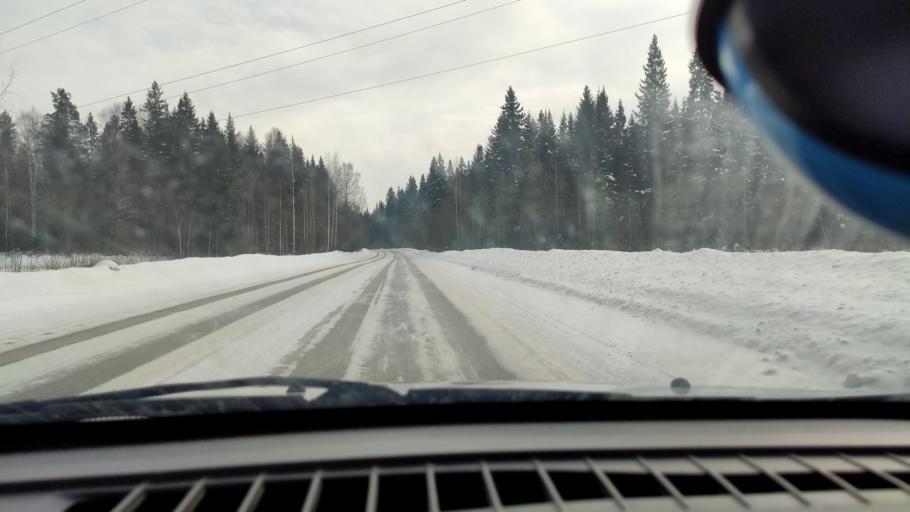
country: RU
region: Perm
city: Overyata
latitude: 58.1064
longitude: 55.8380
